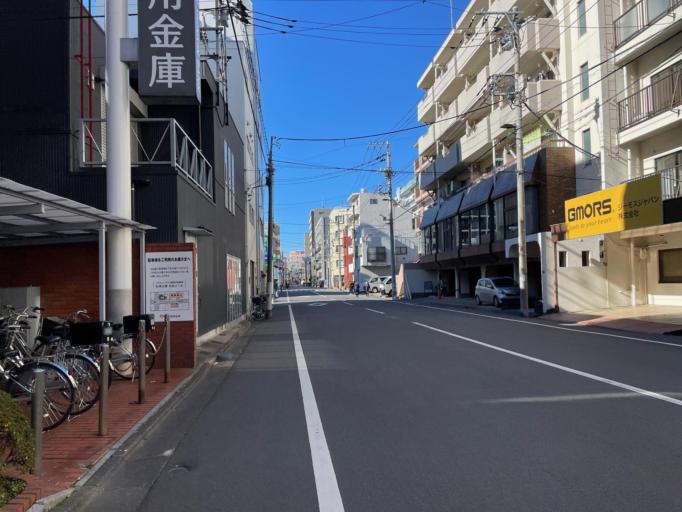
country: JP
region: Tokyo
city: Urayasu
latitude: 35.7020
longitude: 139.7997
